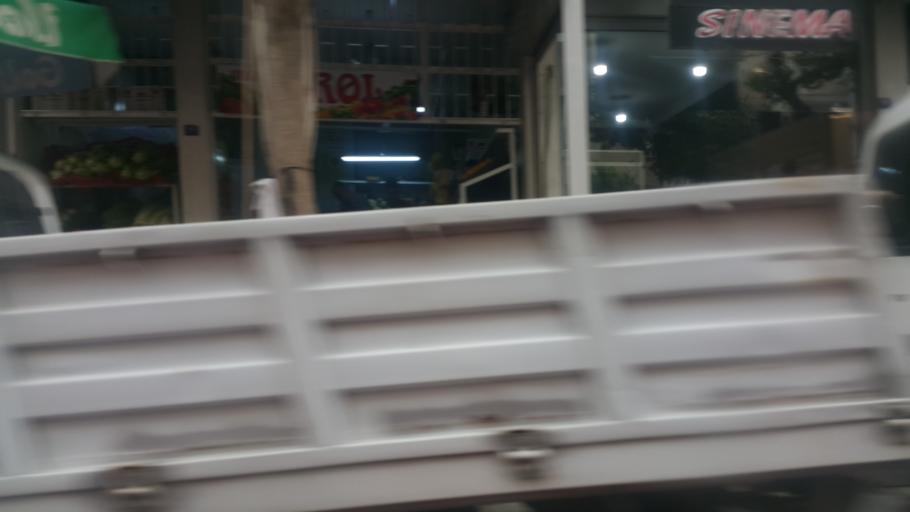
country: TR
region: Mersin
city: Mercin
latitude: 36.7805
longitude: 34.5919
